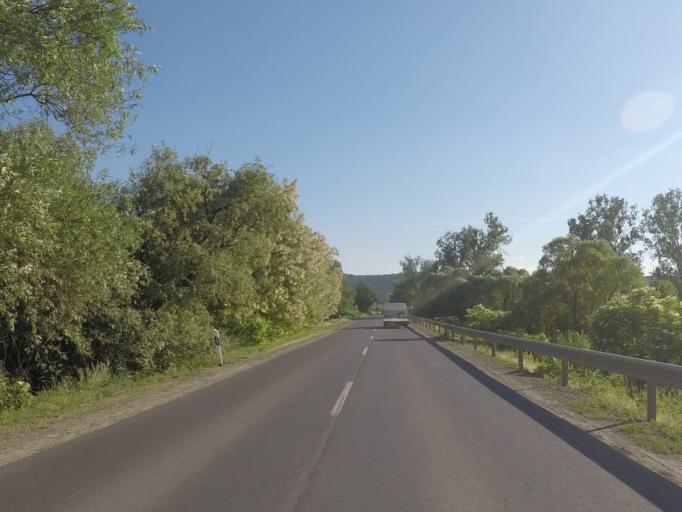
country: HU
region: Borsod-Abauj-Zemplen
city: Kazincbarcika
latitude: 48.2606
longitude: 20.6569
